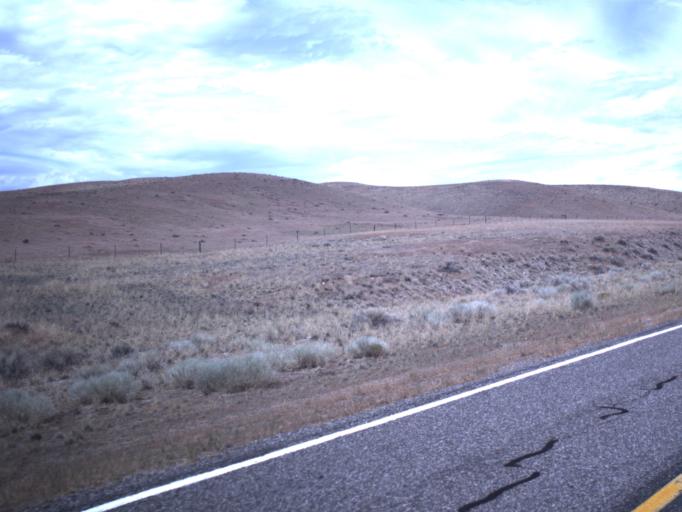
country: US
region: Utah
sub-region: Sevier County
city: Monroe
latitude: 38.6314
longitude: -112.1714
